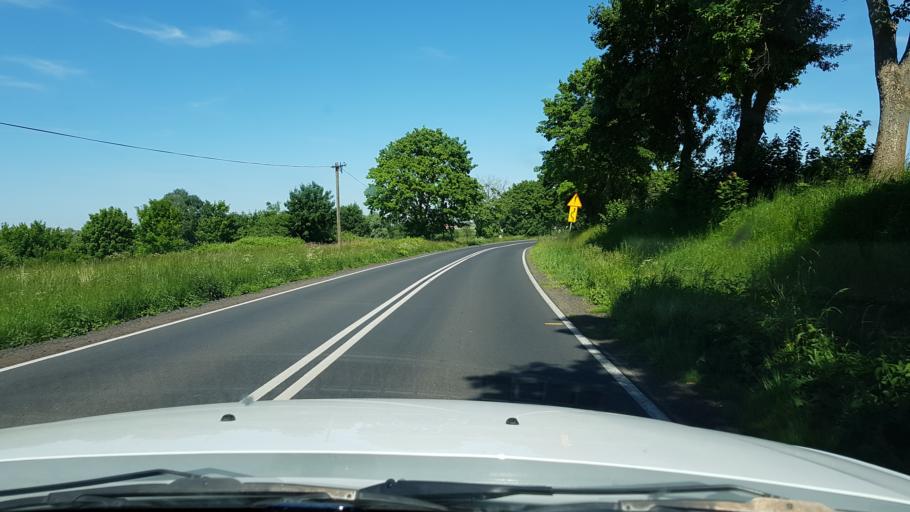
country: PL
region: West Pomeranian Voivodeship
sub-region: Powiat gryfinski
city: Banie
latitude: 53.1175
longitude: 14.7155
